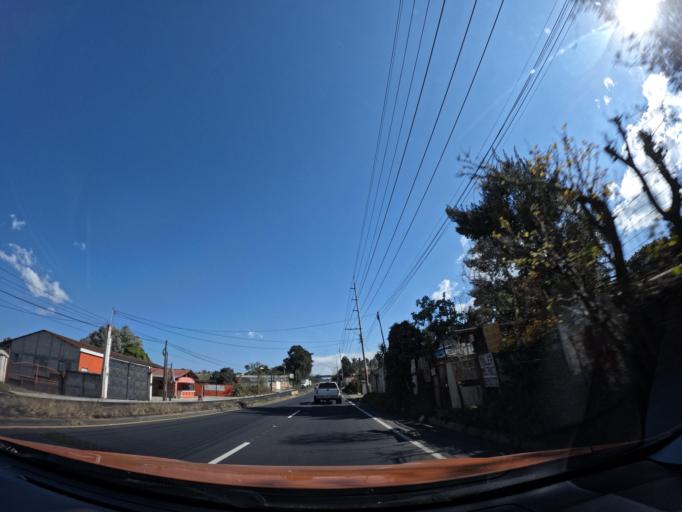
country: GT
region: Sacatepequez
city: Santiago Sacatepequez
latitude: 14.6295
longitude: -90.6874
